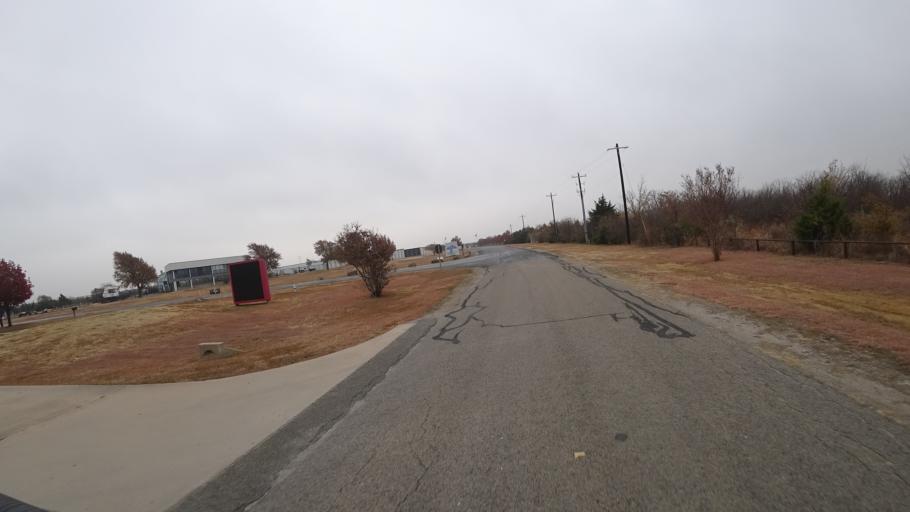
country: US
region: Texas
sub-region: Denton County
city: The Colony
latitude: 33.0723
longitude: -96.9210
